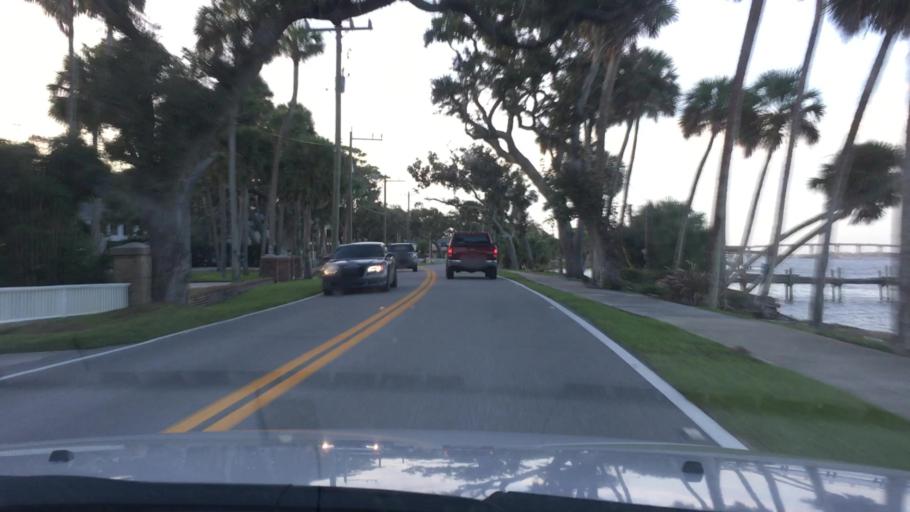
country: US
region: Florida
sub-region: Volusia County
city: Ormond Beach
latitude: 29.2735
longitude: -81.0489
